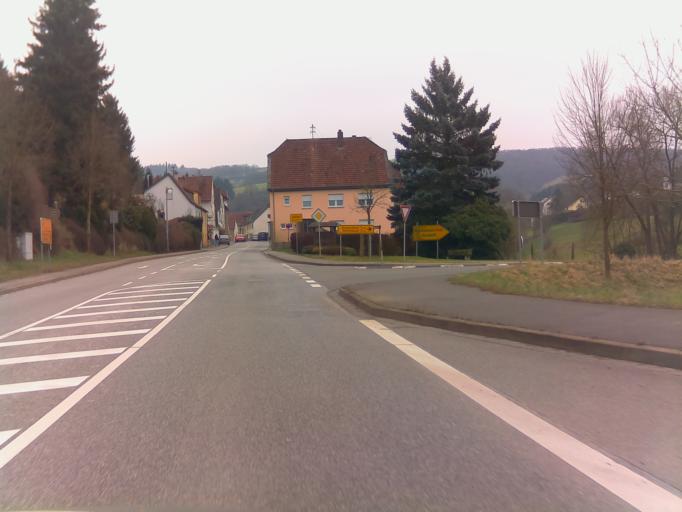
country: DE
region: Rheinland-Pfalz
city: Callbach
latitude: 49.7076
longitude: 7.6940
